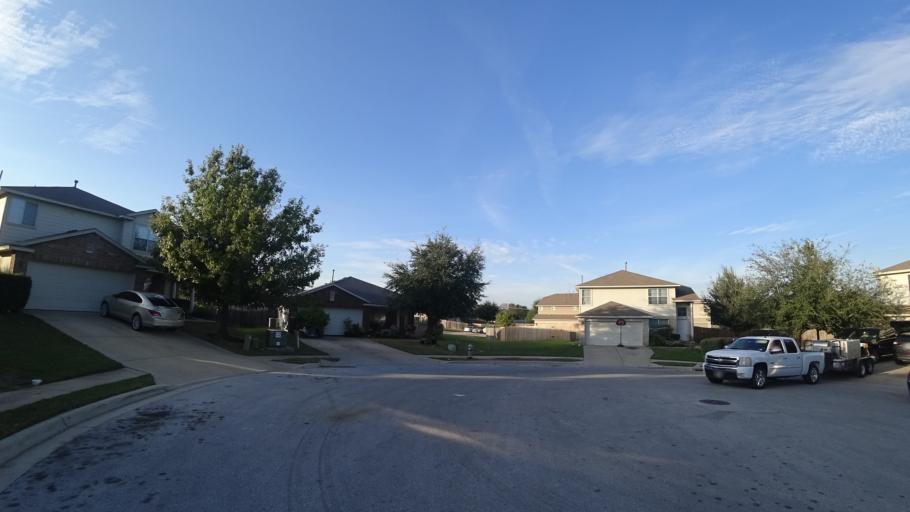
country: US
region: Texas
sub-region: Travis County
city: Pflugerville
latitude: 30.4166
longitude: -97.6456
